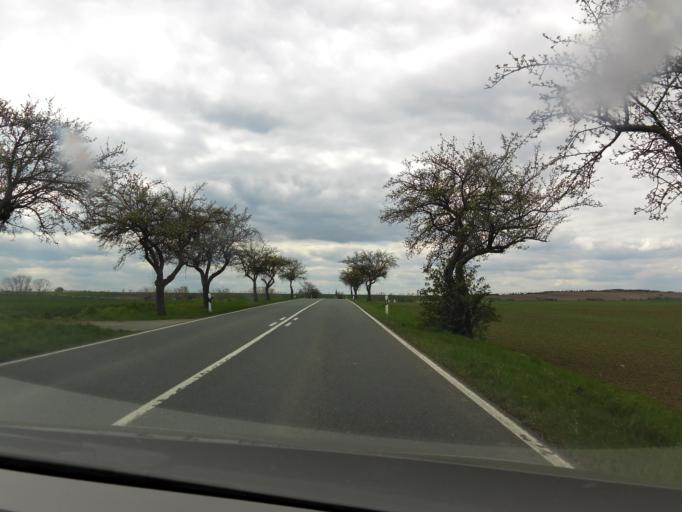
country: DE
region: Thuringia
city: Bad Sulza
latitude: 51.1226
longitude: 11.6224
